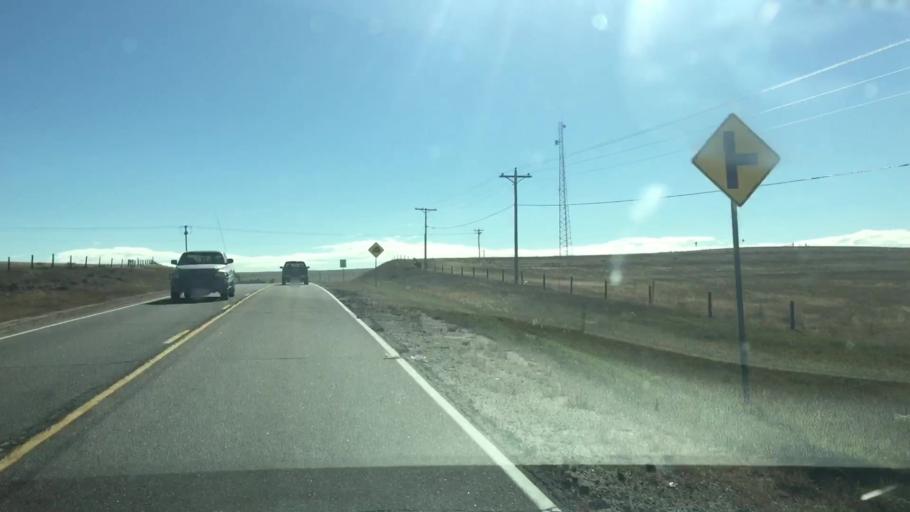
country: US
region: Colorado
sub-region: Elbert County
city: Kiowa
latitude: 39.3489
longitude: -104.4806
